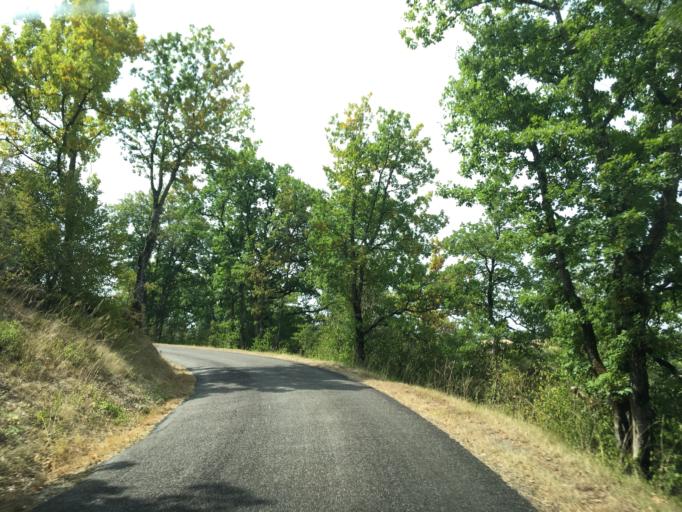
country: FR
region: Midi-Pyrenees
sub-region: Departement du Lot
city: Le Vigan
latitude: 44.7604
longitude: 1.5511
